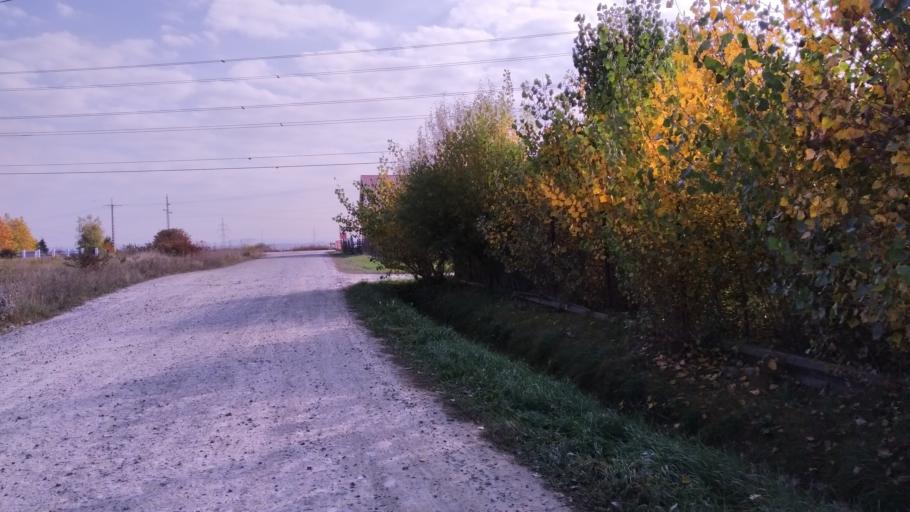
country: HU
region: Pest
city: Pomaz
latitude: 47.6415
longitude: 19.0421
